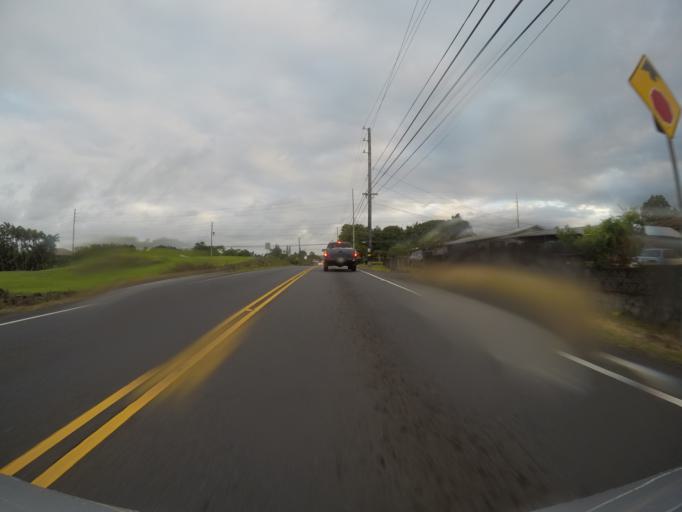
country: US
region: Hawaii
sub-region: Hawaii County
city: Hilo
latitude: 19.6840
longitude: -155.0898
